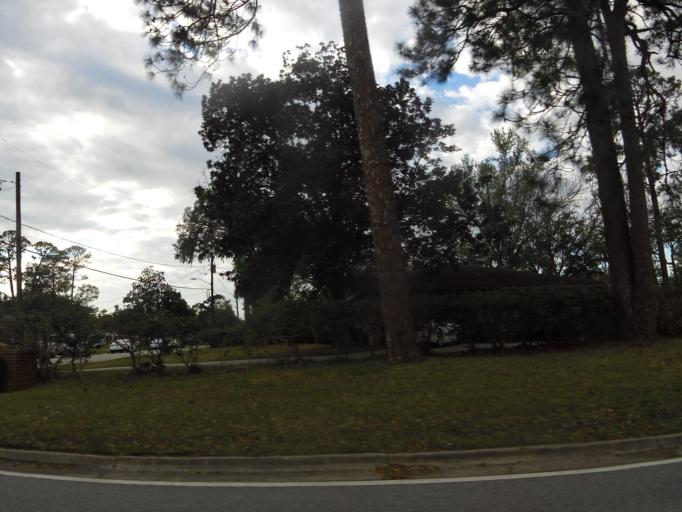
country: US
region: Florida
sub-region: Duval County
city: Jacksonville
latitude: 30.2526
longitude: -81.6318
